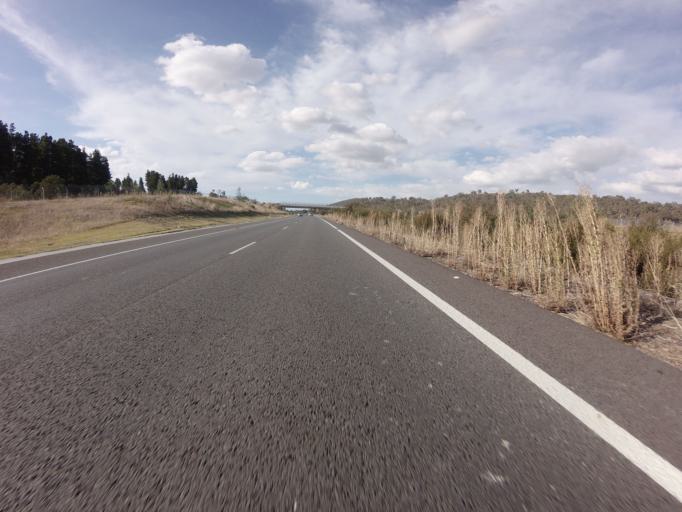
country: AU
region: Australian Capital Territory
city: Canberra
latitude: -35.2363
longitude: 149.1944
